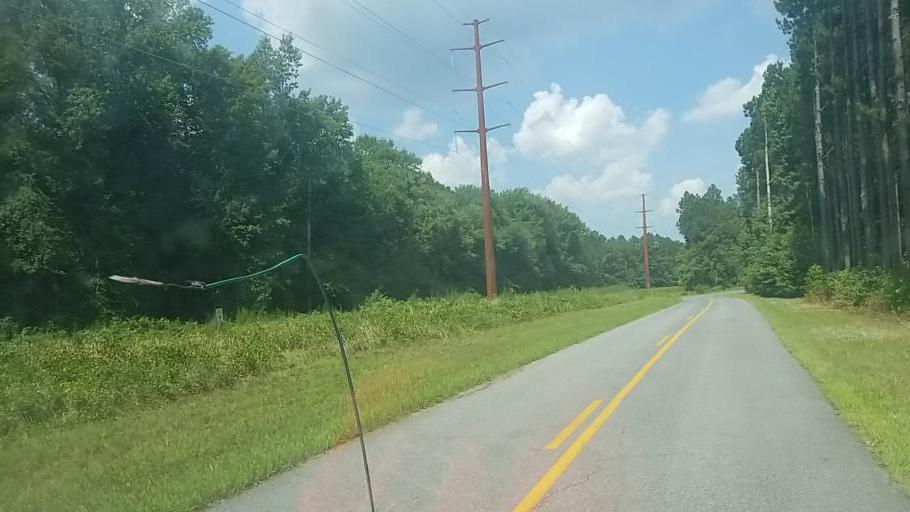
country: US
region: Maryland
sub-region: Worcester County
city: Snow Hill
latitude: 38.2670
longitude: -75.4695
